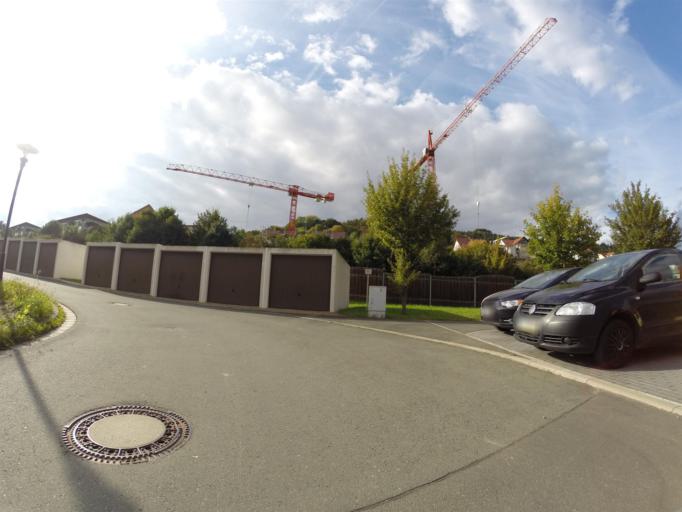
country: DE
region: Thuringia
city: Neuengonna
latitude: 50.9616
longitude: 11.6225
